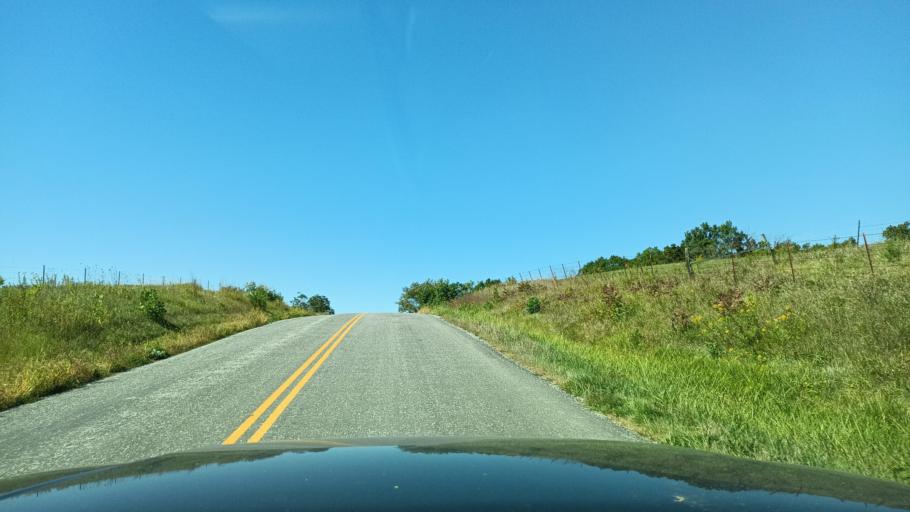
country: US
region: Missouri
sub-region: Adair County
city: Kirksville
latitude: 40.3300
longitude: -92.5466
